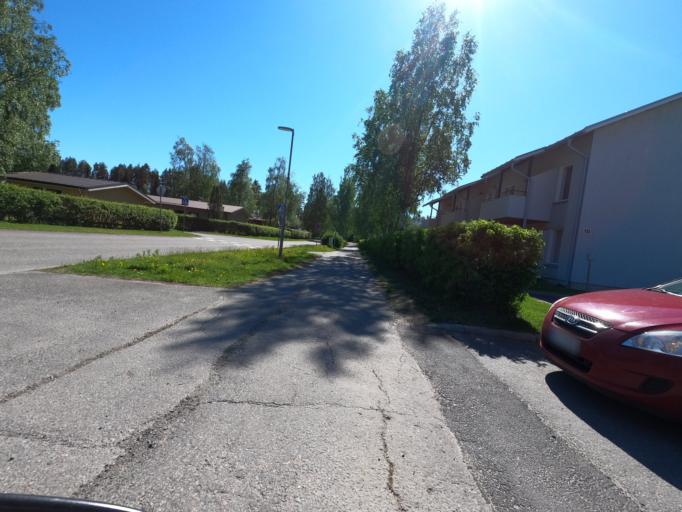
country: FI
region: North Karelia
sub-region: Joensuu
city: Joensuu
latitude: 62.5970
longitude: 29.8054
